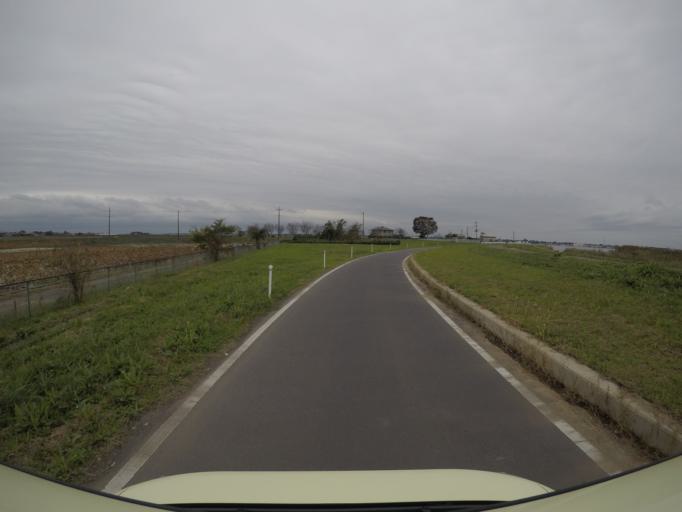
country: JP
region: Ibaraki
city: Ami
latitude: 36.0740
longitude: 140.2417
